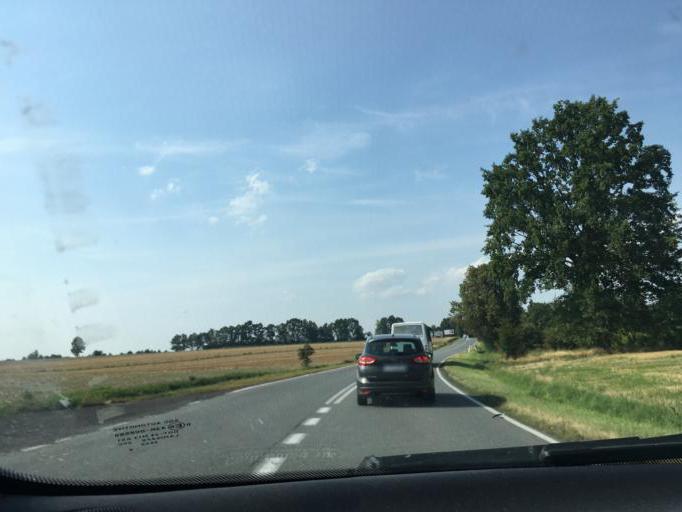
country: PL
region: Opole Voivodeship
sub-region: Powiat prudnicki
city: Laka Prudnicka
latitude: 50.3665
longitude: 17.5393
